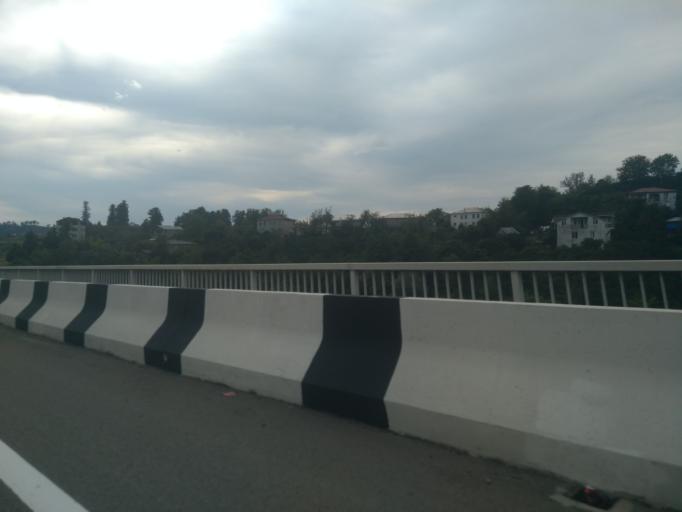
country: GE
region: Ajaria
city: Makhinjauri
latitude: 41.7119
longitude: 41.7506
